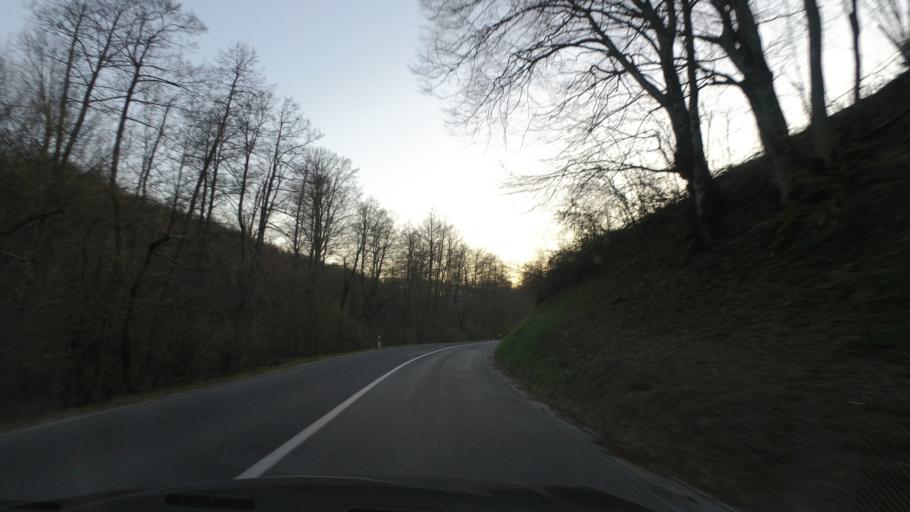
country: HR
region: Karlovacka
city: Vojnic
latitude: 45.3398
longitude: 15.7632
